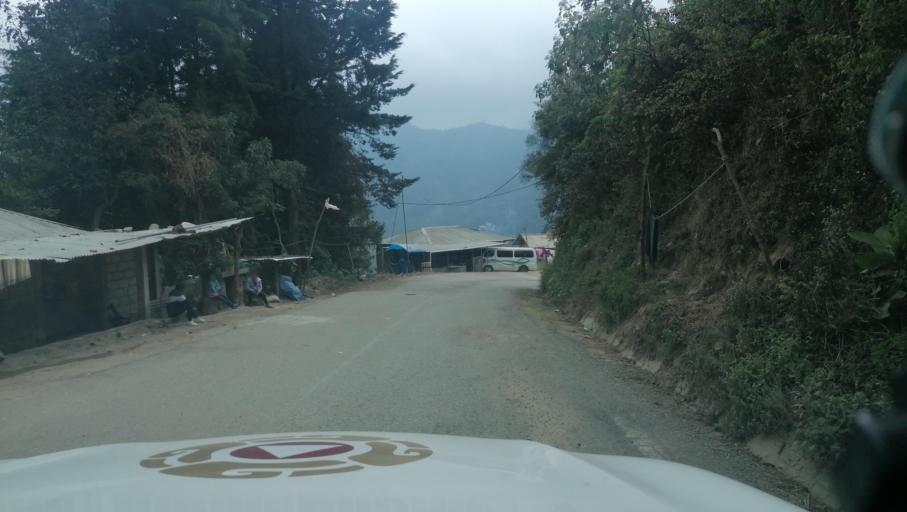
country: GT
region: San Marcos
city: Tacana
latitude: 15.2045
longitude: -92.1874
